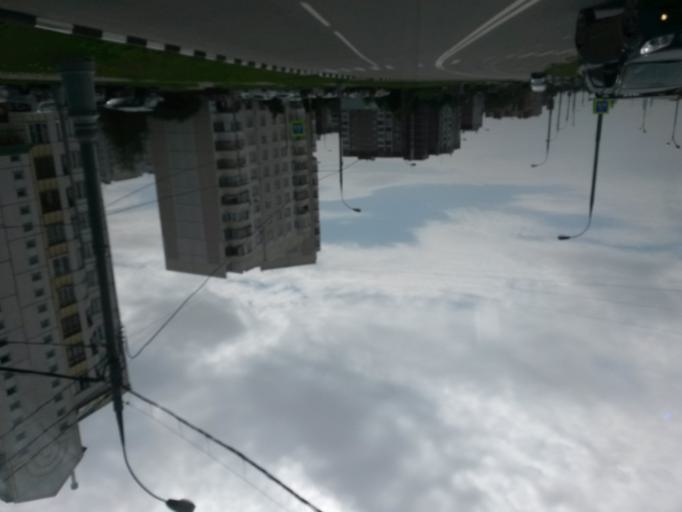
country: RU
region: Moskovskaya
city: Shcherbinka
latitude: 55.5397
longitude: 37.5332
